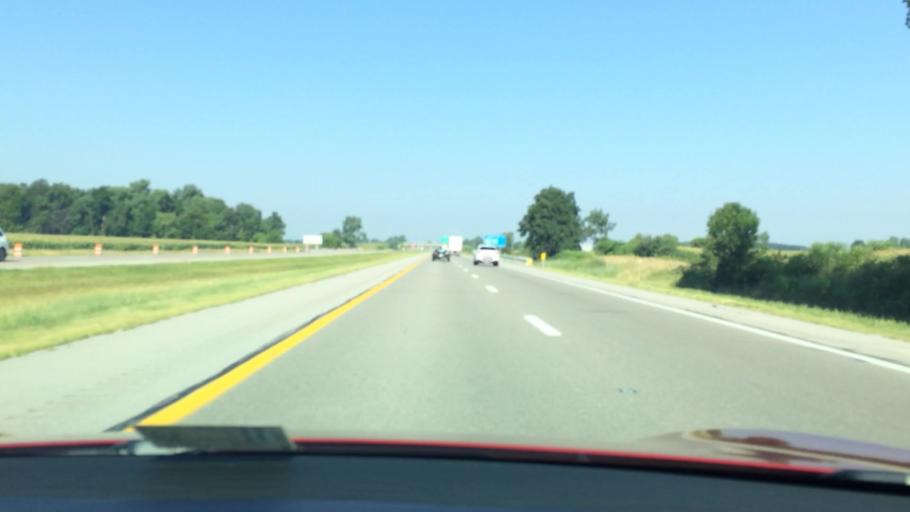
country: US
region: Ohio
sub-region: Fulton County
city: Wauseon
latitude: 41.5917
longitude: -84.1221
